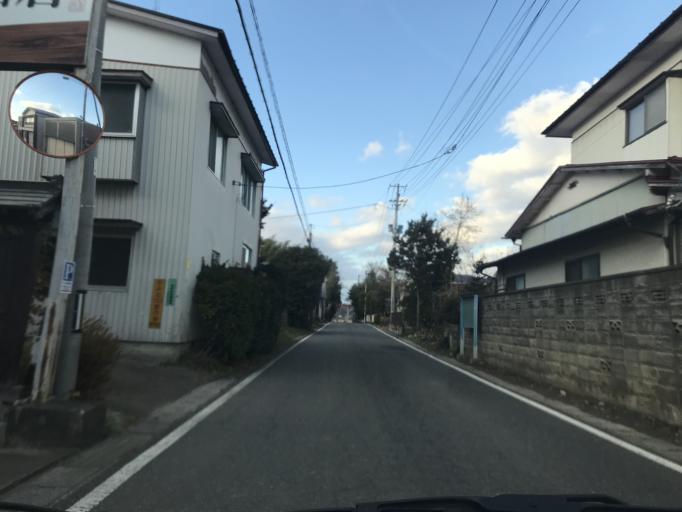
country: JP
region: Miyagi
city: Kogota
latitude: 38.6413
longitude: 141.0520
